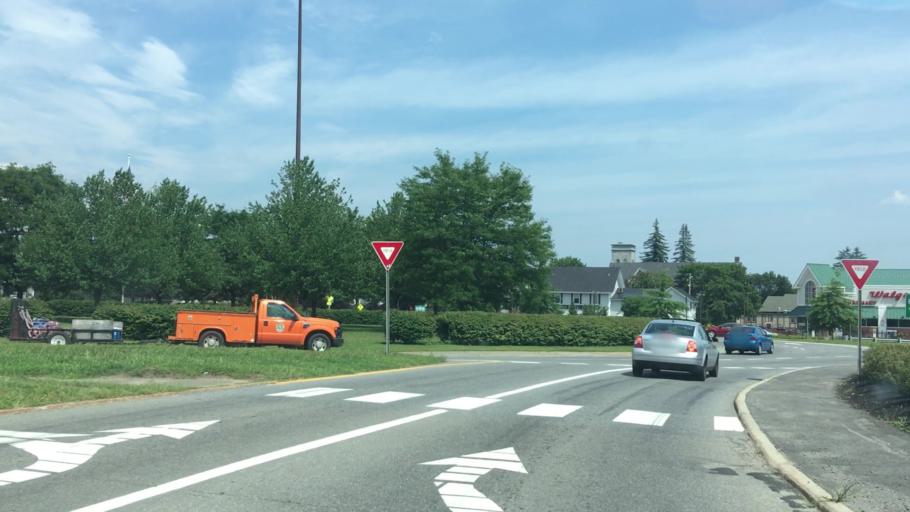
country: US
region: Maine
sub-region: Kennebec County
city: Augusta
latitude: 44.3100
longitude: -69.7796
